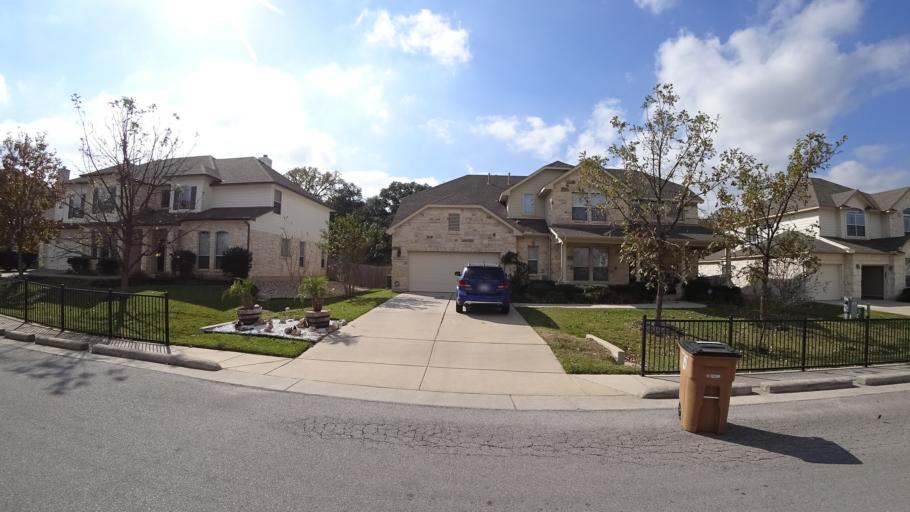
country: US
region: Texas
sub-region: Travis County
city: Shady Hollow
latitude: 30.1607
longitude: -97.8478
